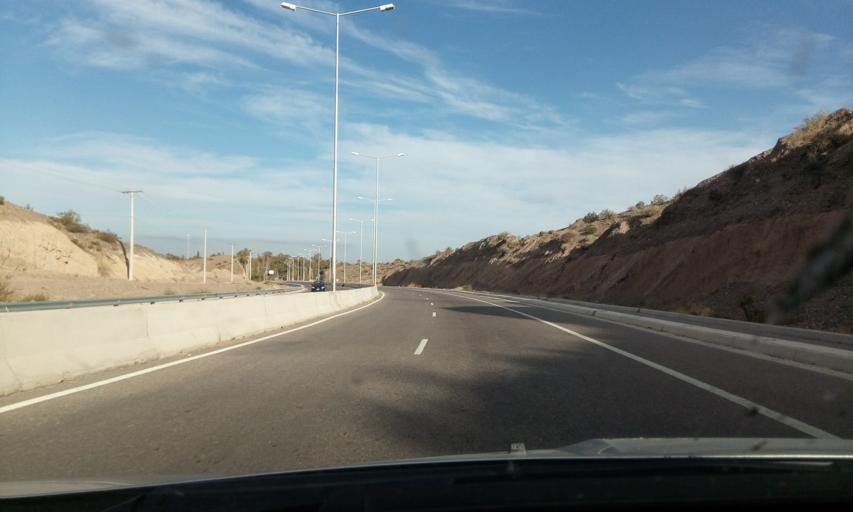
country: AR
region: San Juan
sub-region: Departamento de Rivadavia
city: Rivadavia
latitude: -31.5004
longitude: -68.6487
